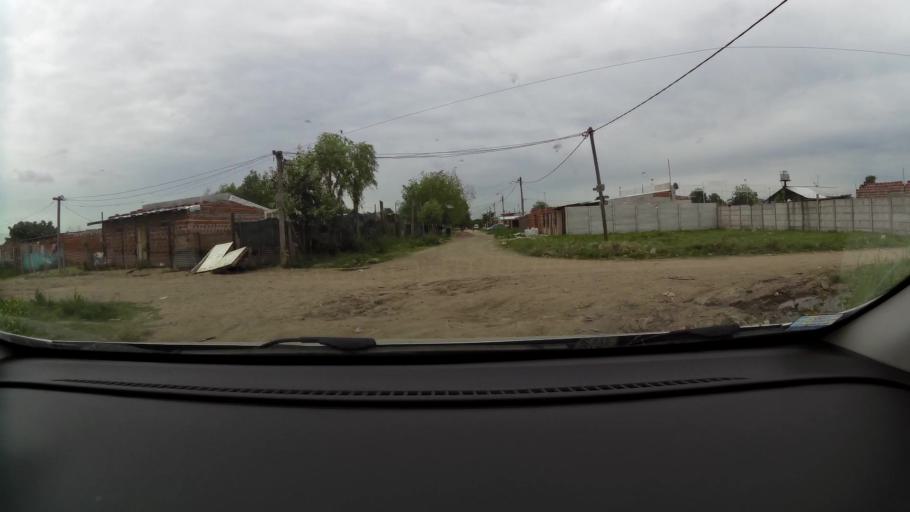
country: AR
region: Buenos Aires
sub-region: Partido de Zarate
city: Zarate
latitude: -34.1183
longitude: -59.0331
